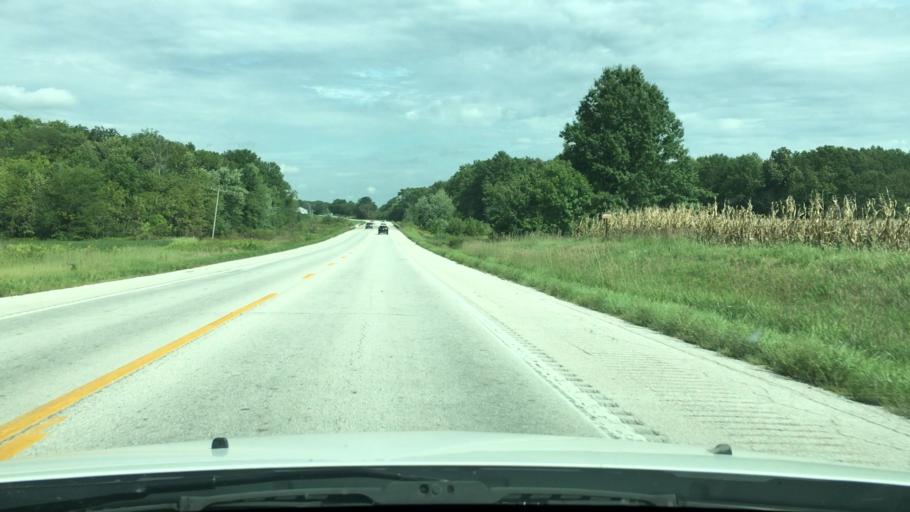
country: US
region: Missouri
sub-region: Montgomery County
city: Wellsville
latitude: 39.1976
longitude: -91.6465
